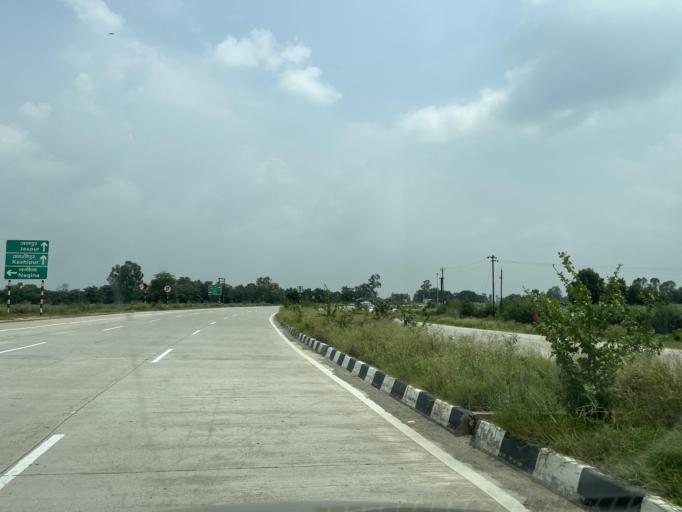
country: IN
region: Uttar Pradesh
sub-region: Bijnor
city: Nagina
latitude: 29.4253
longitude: 78.4405
